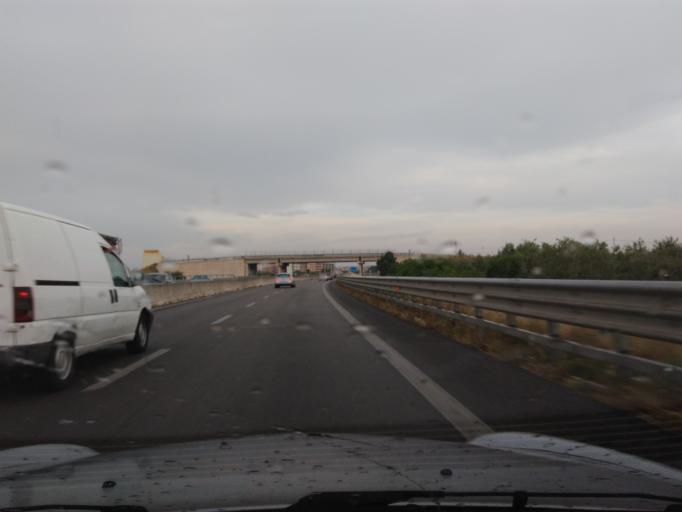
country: IT
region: Apulia
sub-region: Provincia di Bari
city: Molfetta
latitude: 41.2010
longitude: 16.5743
